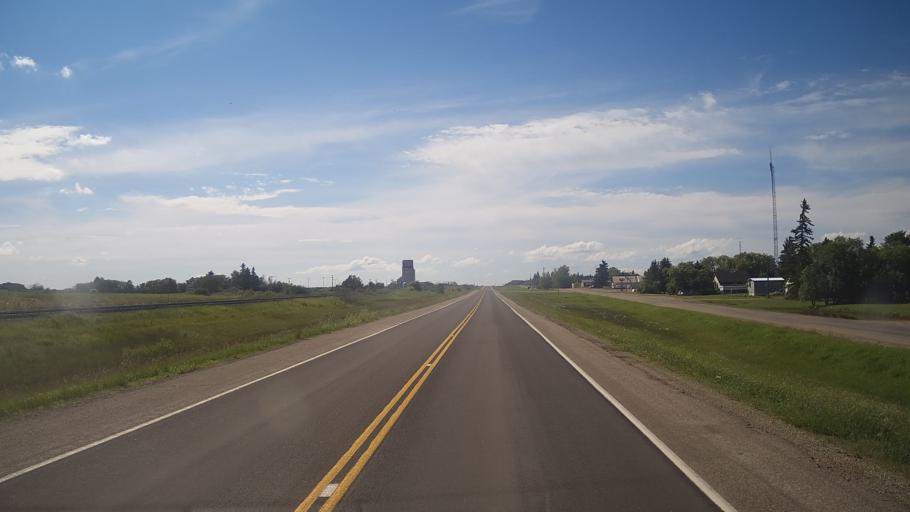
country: CA
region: Saskatchewan
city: Foam Lake
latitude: 51.2607
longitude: -103.7325
